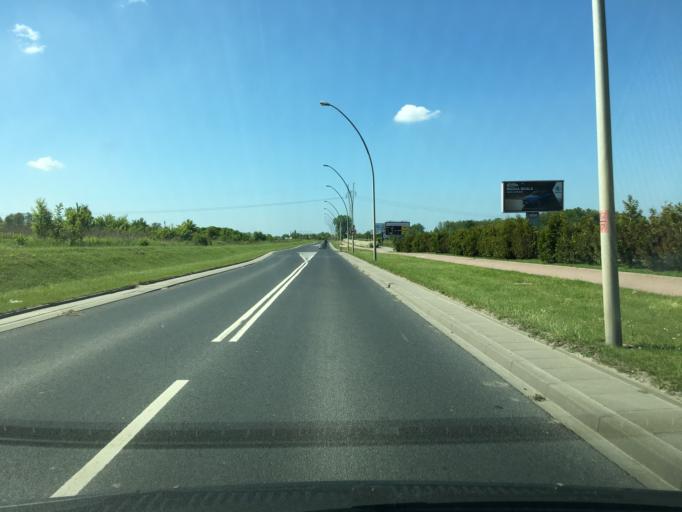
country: PL
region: Lower Silesian Voivodeship
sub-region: Powiat wroclawski
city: Bielany Wroclawskie
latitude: 51.0547
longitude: 16.9610
